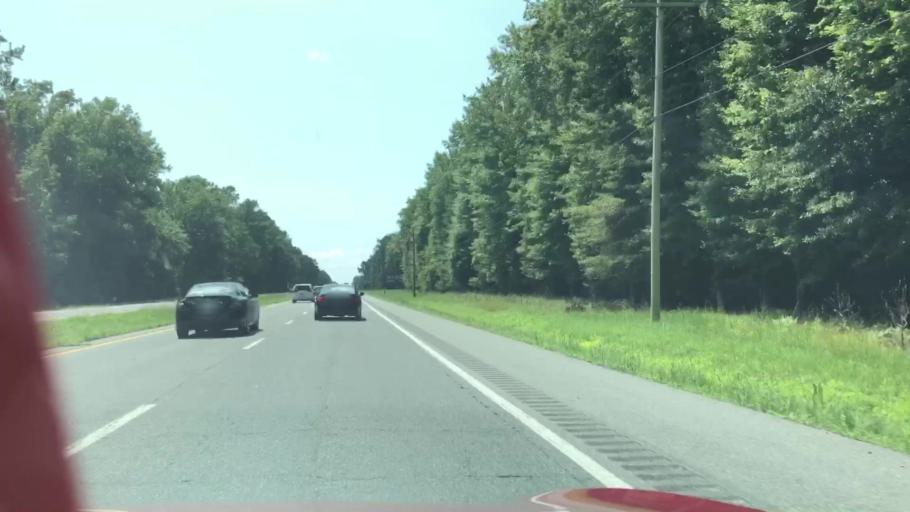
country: US
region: Virginia
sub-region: Northampton County
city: Cape Charles
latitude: 37.2014
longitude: -75.9670
